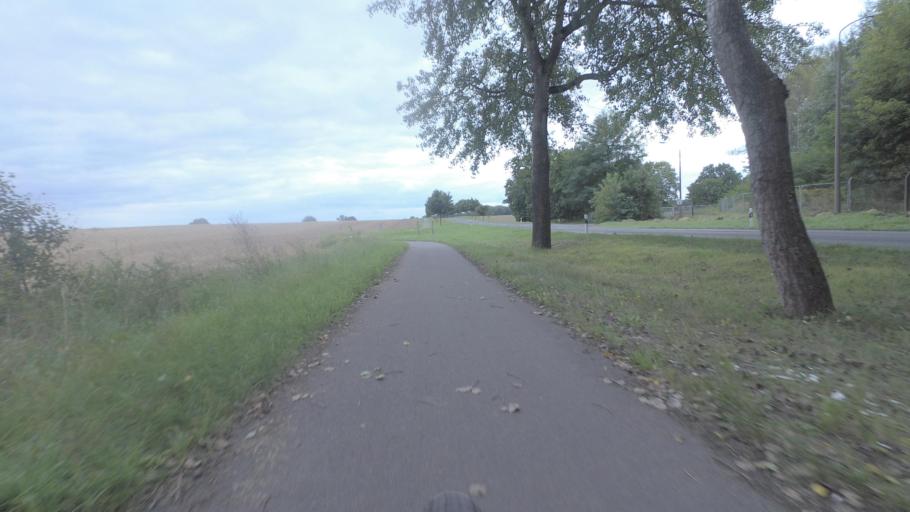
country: DE
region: Brandenburg
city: Werneuchen
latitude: 52.6078
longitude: 13.6829
